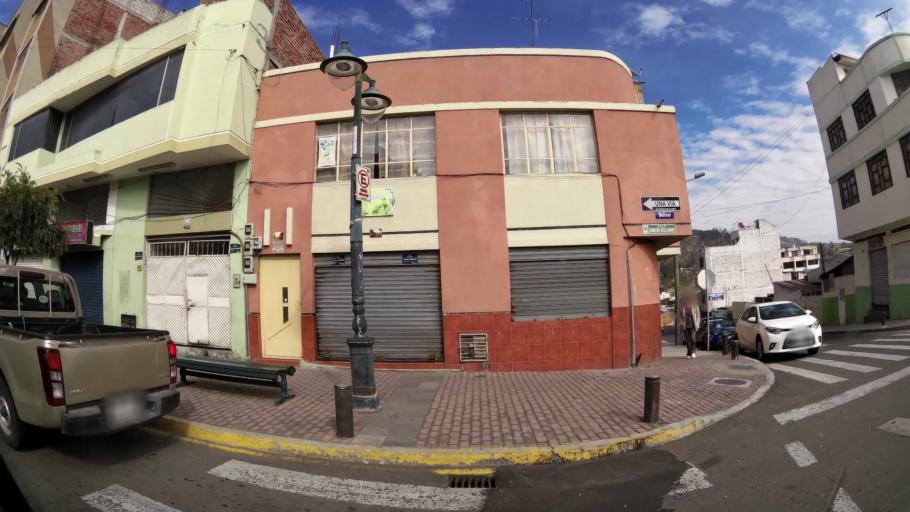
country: EC
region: Tungurahua
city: Ambato
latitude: -1.2522
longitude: -78.6424
